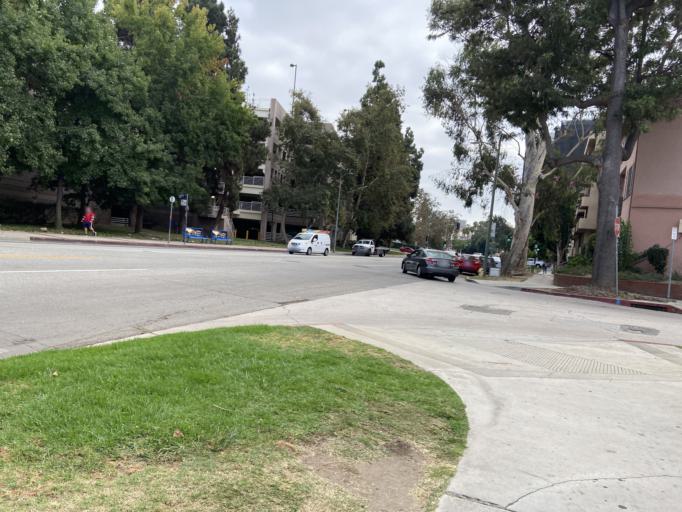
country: US
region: California
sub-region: Los Angeles County
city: Westwood, Los Angeles
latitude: 34.0658
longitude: -118.4478
